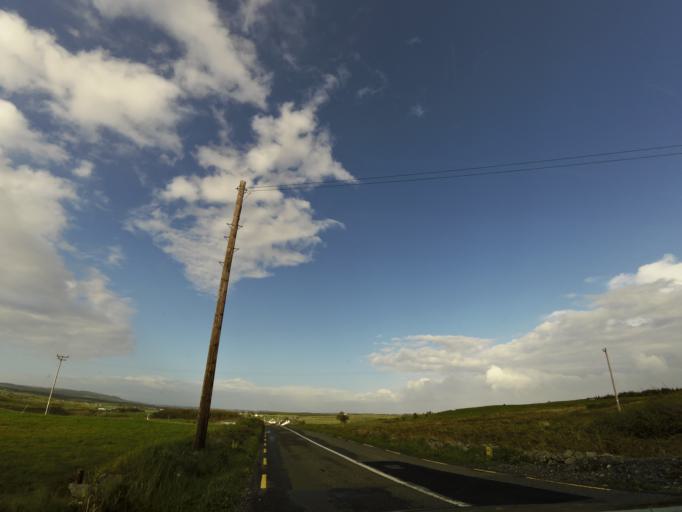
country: IE
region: Connaught
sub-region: County Galway
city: Bearna
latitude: 53.0153
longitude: -9.3251
